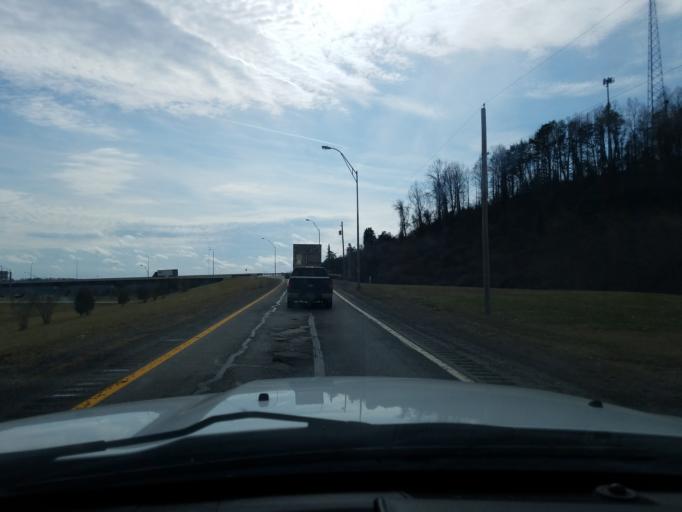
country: US
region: West Virginia
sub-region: Putnam County
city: Teays Valley
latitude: 38.4569
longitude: -81.9052
